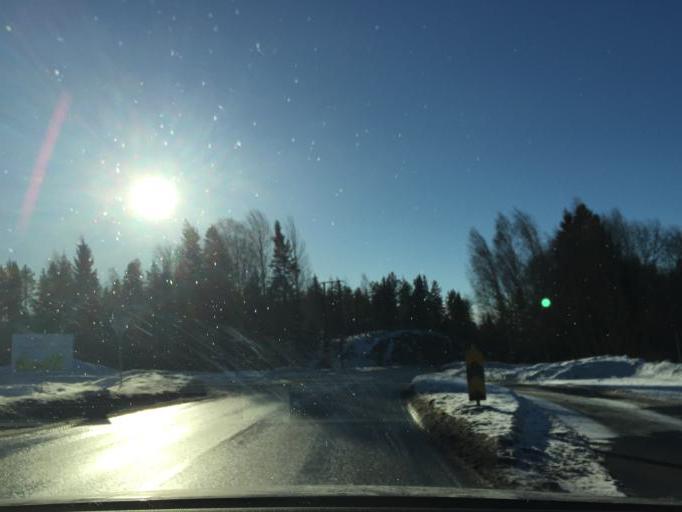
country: NO
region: Akershus
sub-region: Nes
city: Arnes
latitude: 60.1767
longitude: 11.5373
